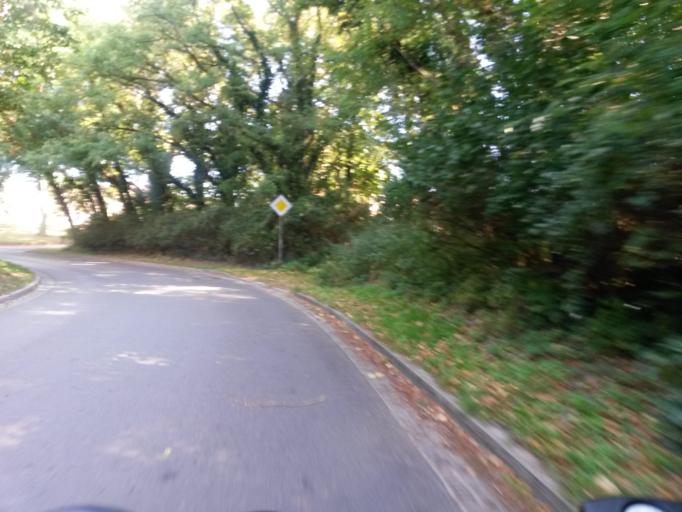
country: DE
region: Brandenburg
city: Templin
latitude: 53.1709
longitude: 13.4421
